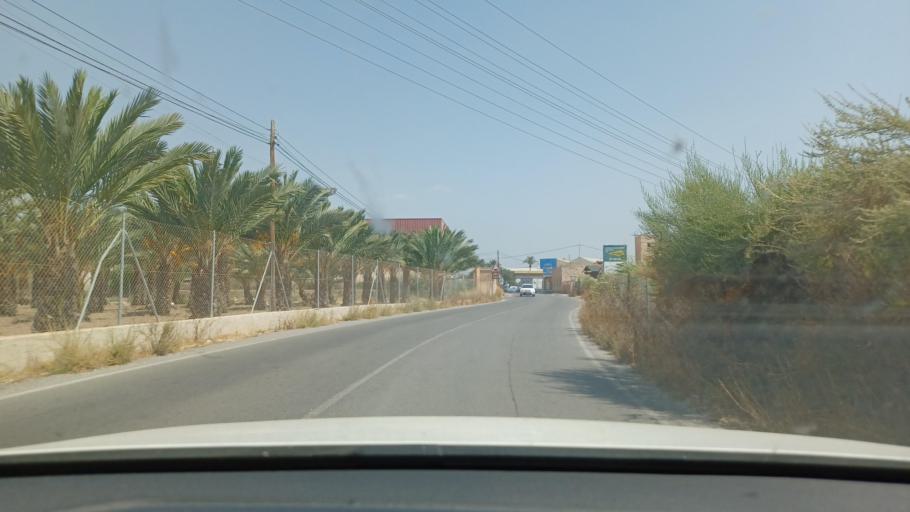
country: ES
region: Valencia
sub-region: Provincia de Alicante
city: Elche
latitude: 38.2489
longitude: -0.6915
